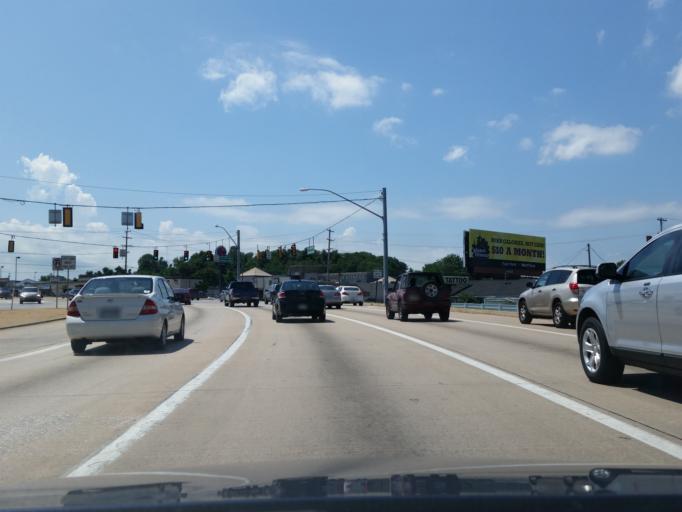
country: US
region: Pennsylvania
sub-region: York County
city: North York
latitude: 39.9843
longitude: -76.7366
